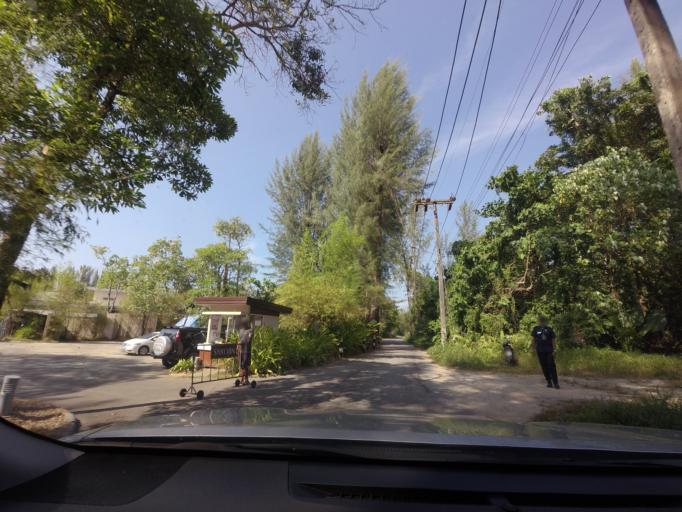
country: TH
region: Phangnga
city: Ban Khao Lak
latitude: 8.7344
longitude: 98.2425
